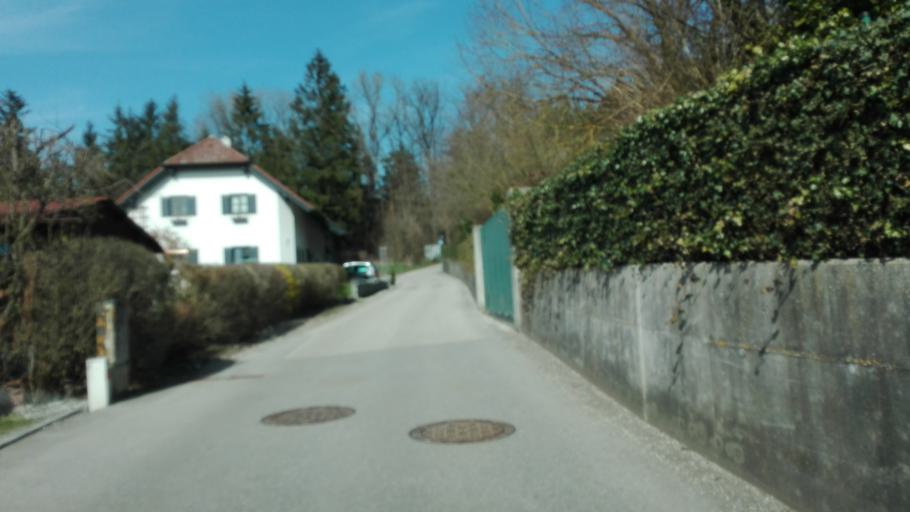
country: AT
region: Lower Austria
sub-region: Politischer Bezirk Amstetten
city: Ennsdorf
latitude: 48.2491
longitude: 14.5110
